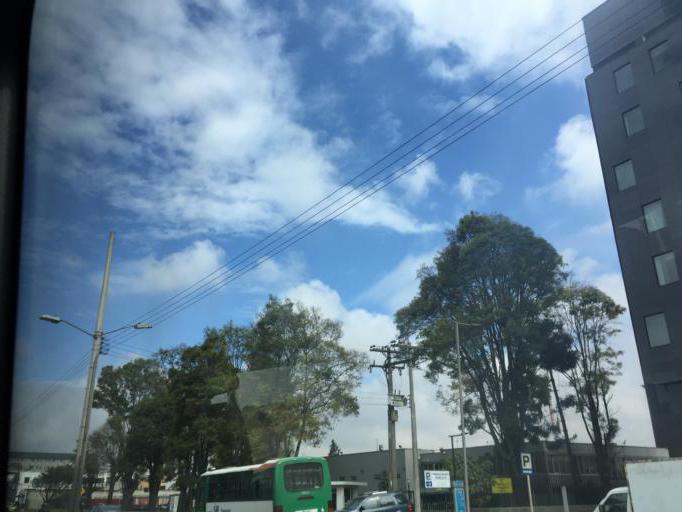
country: CO
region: Cundinamarca
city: Funza
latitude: 4.6872
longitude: -74.1276
